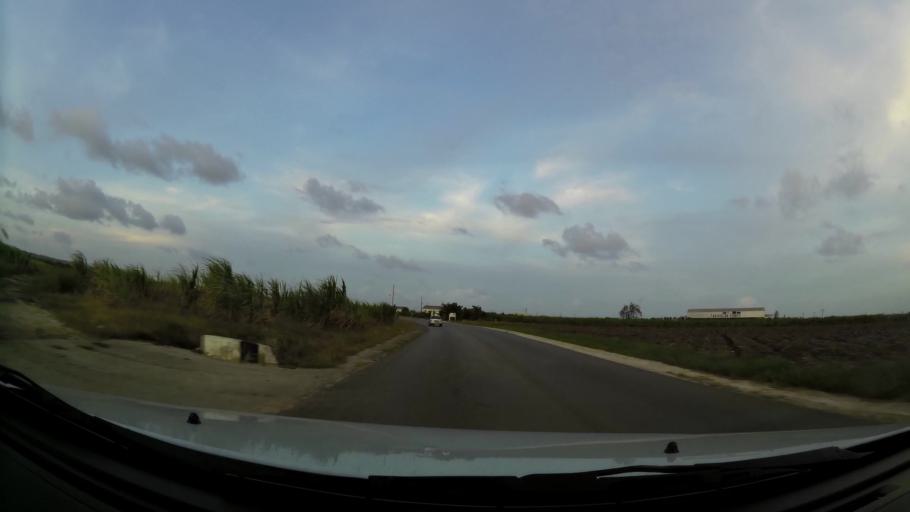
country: BB
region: Saint Philip
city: Crane
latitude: 13.1120
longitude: -59.4807
